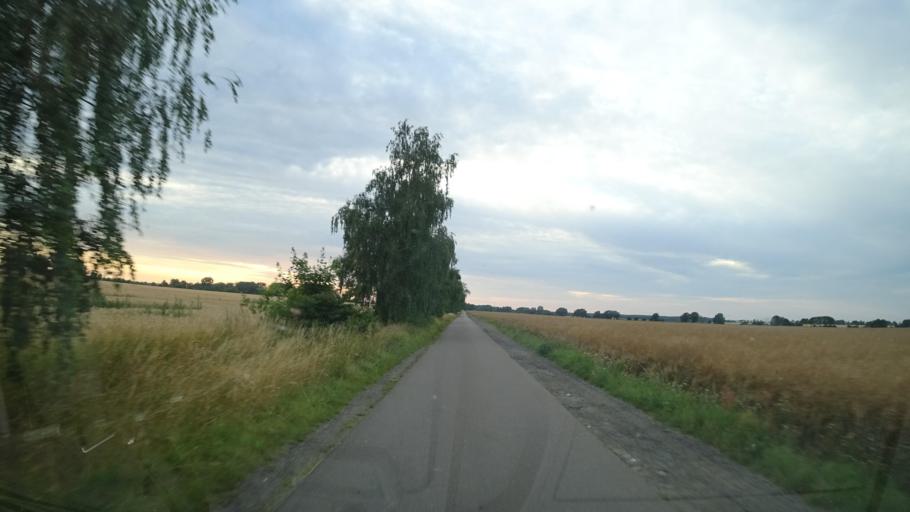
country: DE
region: Mecklenburg-Vorpommern
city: Kemnitz
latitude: 54.0918
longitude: 13.5276
